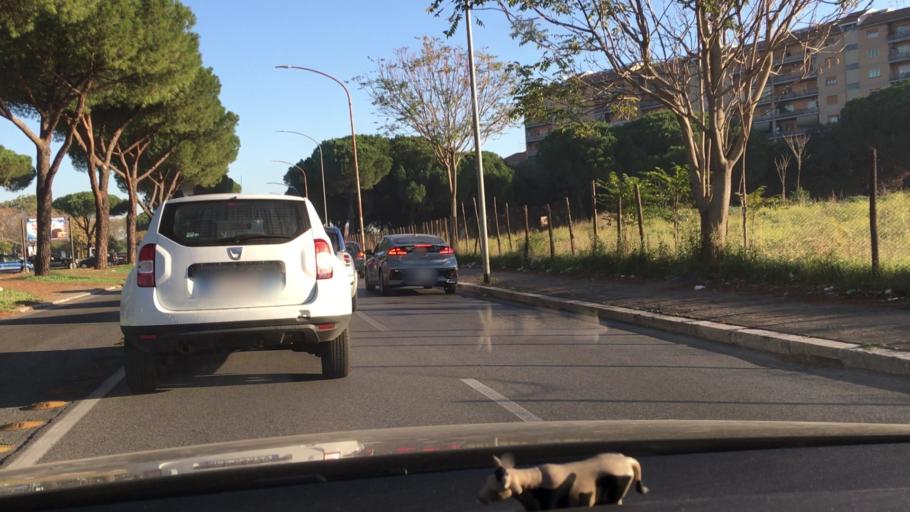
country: IT
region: Latium
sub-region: Citta metropolitana di Roma Capitale
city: Rome
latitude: 41.8678
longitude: 12.5680
